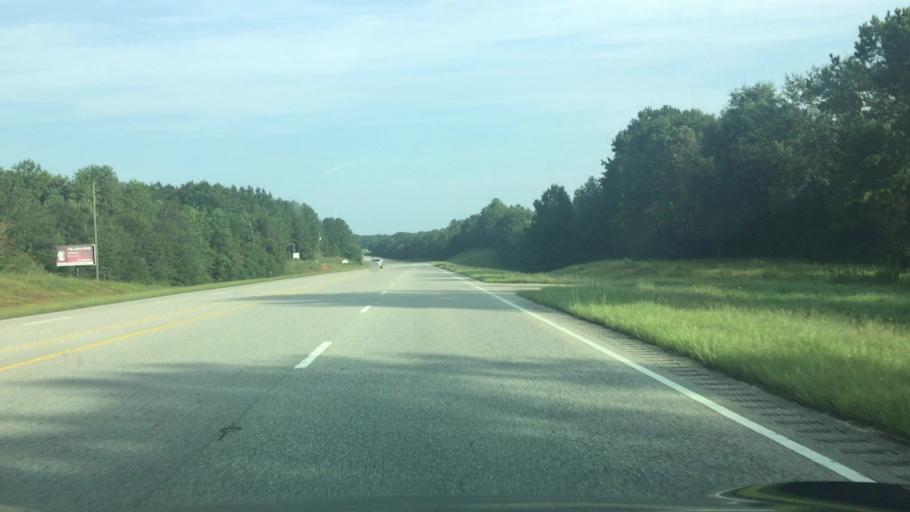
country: US
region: Alabama
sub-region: Butler County
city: Georgiana
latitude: 31.4922
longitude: -86.6865
